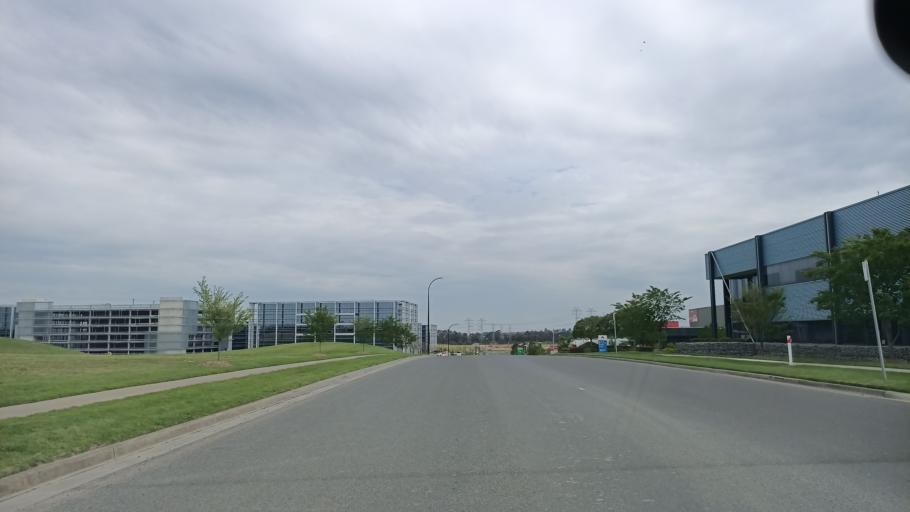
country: AU
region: Victoria
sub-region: Knox
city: Scoresby
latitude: -37.9099
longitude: 145.2183
